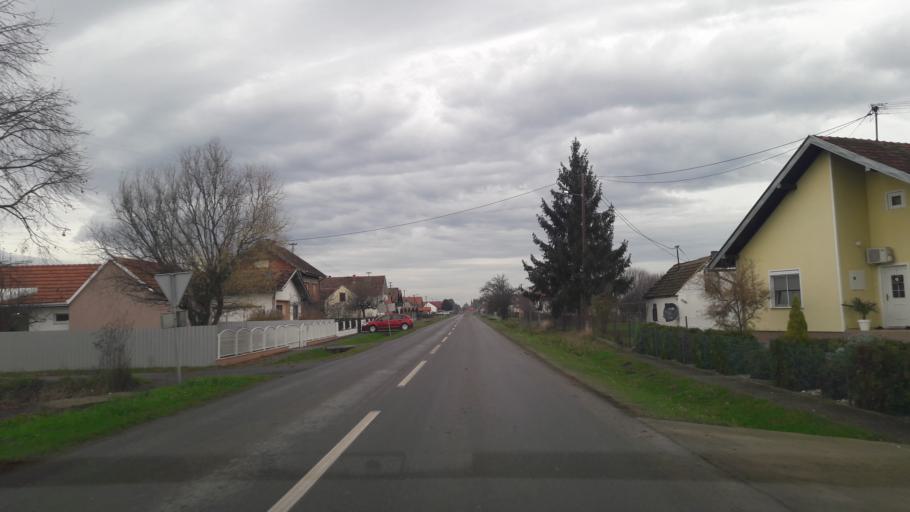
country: HR
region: Osjecko-Baranjska
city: Velimirovac
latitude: 45.5267
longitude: 18.0960
